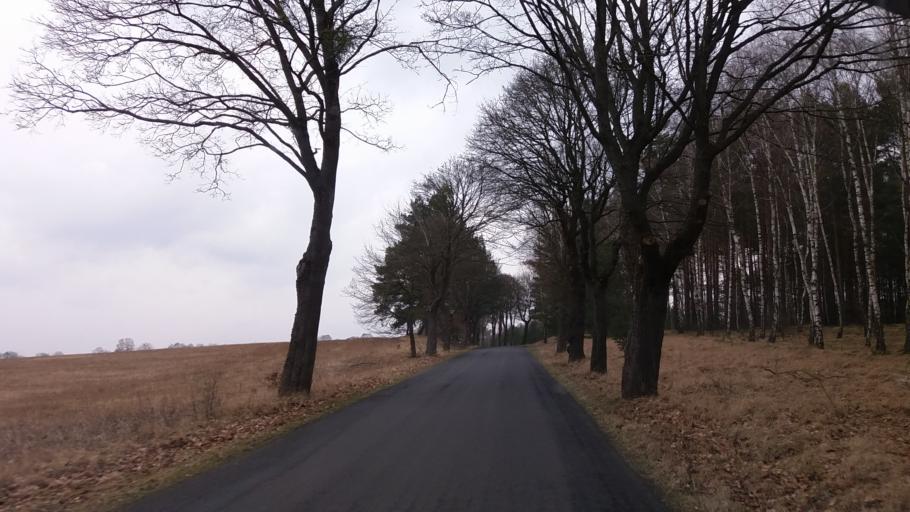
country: PL
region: West Pomeranian Voivodeship
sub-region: Powiat choszczenski
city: Drawno
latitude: 53.1658
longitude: 15.6857
